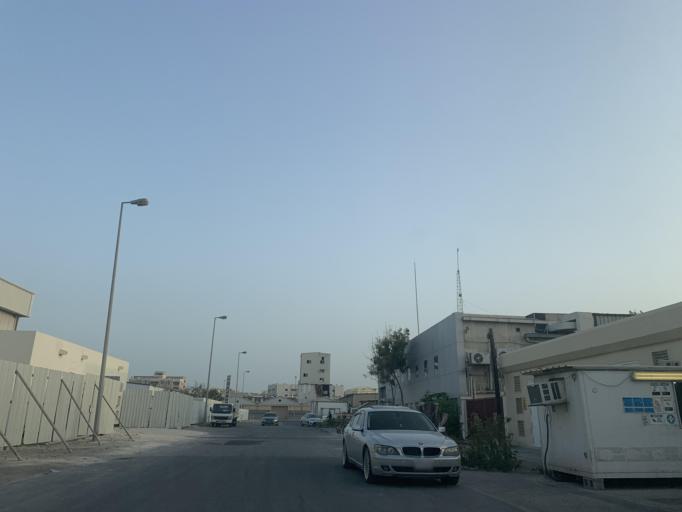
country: BH
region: Manama
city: Manama
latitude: 26.1960
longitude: 50.5939
